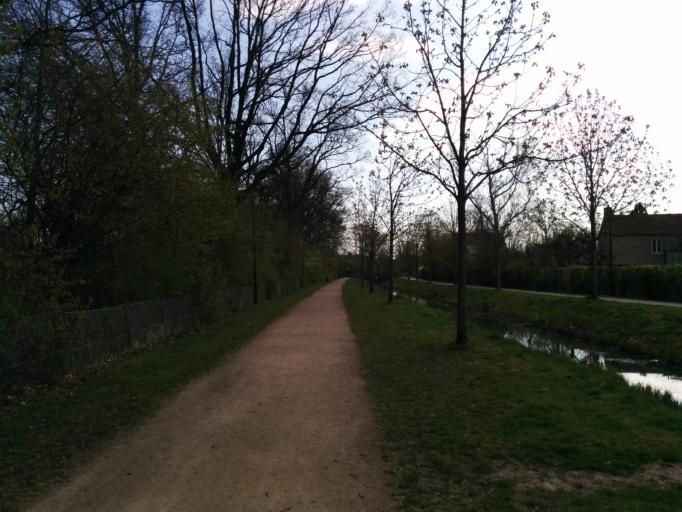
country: DK
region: Capital Region
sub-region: Frederiksberg Kommune
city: Frederiksberg
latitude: 55.7285
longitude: 12.5351
